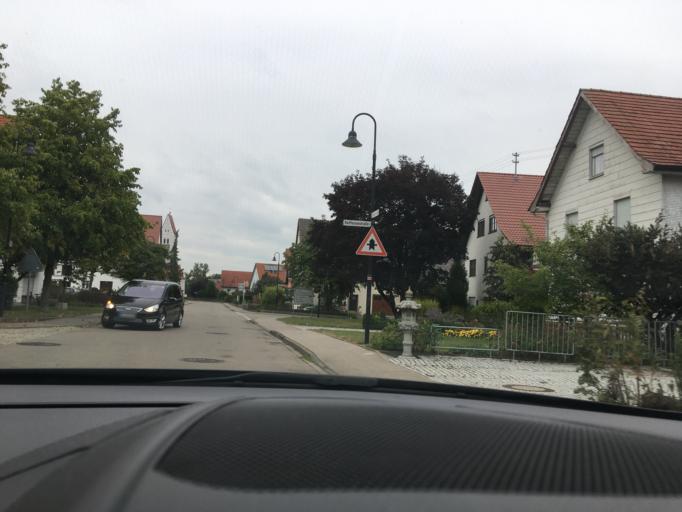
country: DE
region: Baden-Wuerttemberg
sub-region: Tuebingen Region
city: Kirchdorf
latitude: 48.0761
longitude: 10.1270
